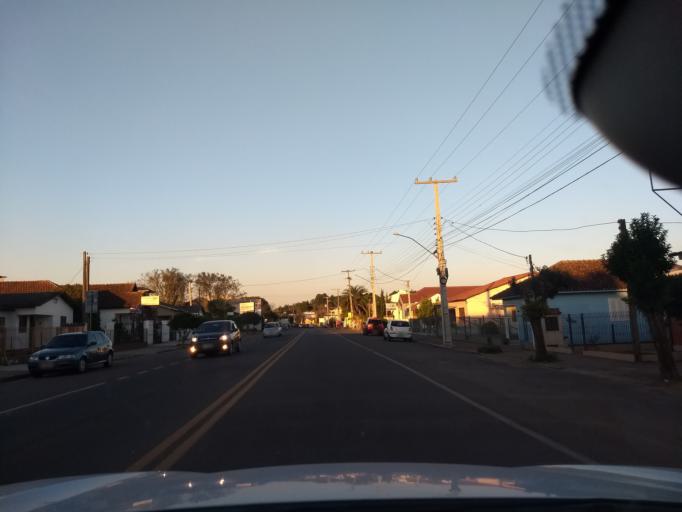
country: BR
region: Rio Grande do Sul
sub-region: Santa Cruz Do Sul
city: Santa Cruz do Sul
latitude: -29.7196
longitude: -52.5154
